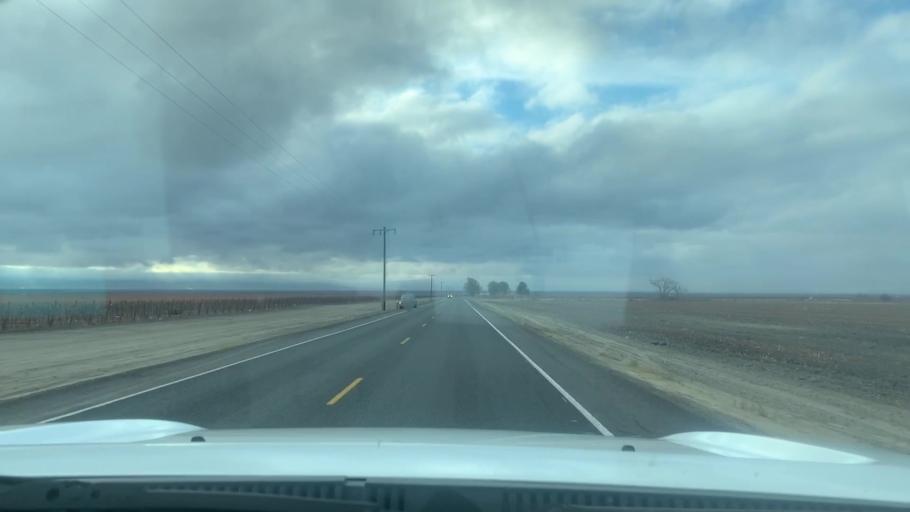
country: US
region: California
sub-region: Kern County
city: Buttonwillow
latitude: 35.4996
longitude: -119.5688
